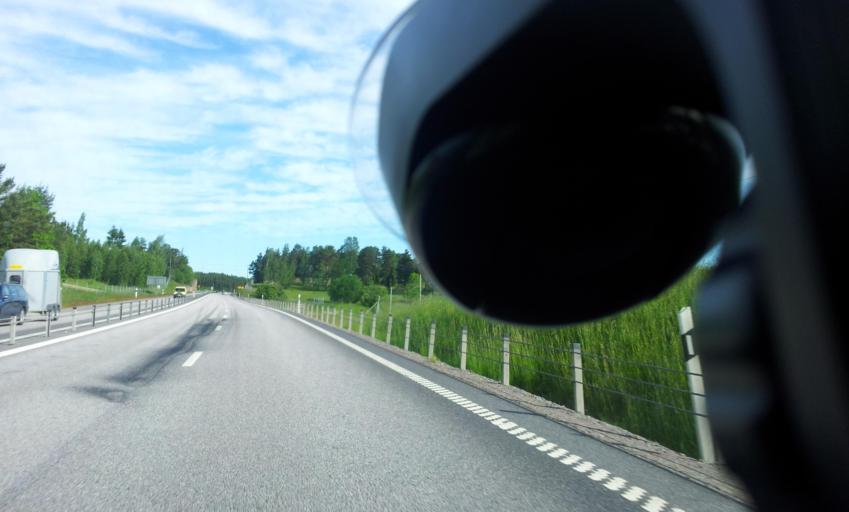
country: SE
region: OEstergoetland
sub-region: Valdemarsviks Kommun
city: Gusum
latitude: 58.3569
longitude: 16.4435
